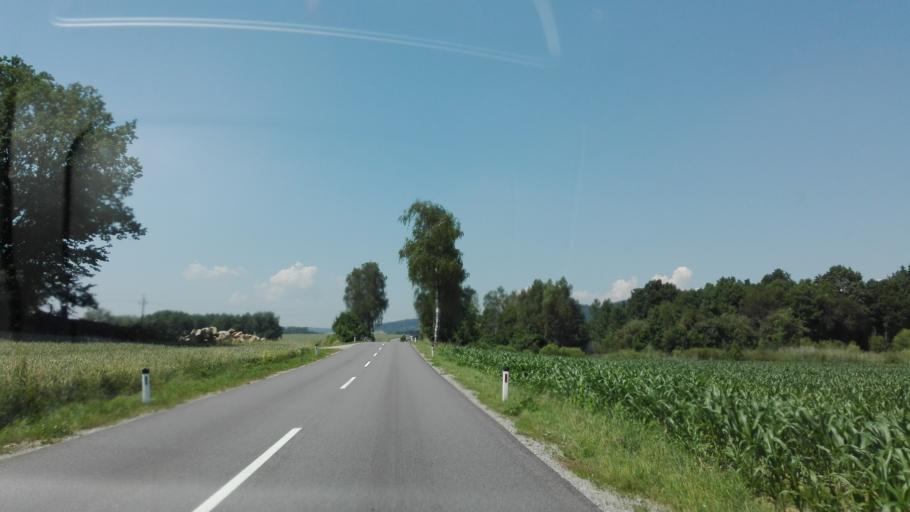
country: AT
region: Upper Austria
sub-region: Politischer Bezirk Grieskirchen
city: Grieskirchen
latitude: 48.3524
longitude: 13.8674
